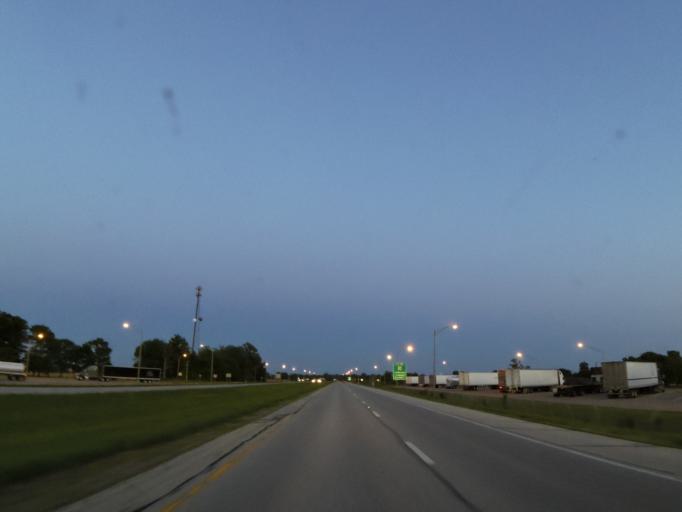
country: US
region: Indiana
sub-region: Hendricks County
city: Pittsboro
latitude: 39.9012
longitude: -86.5553
